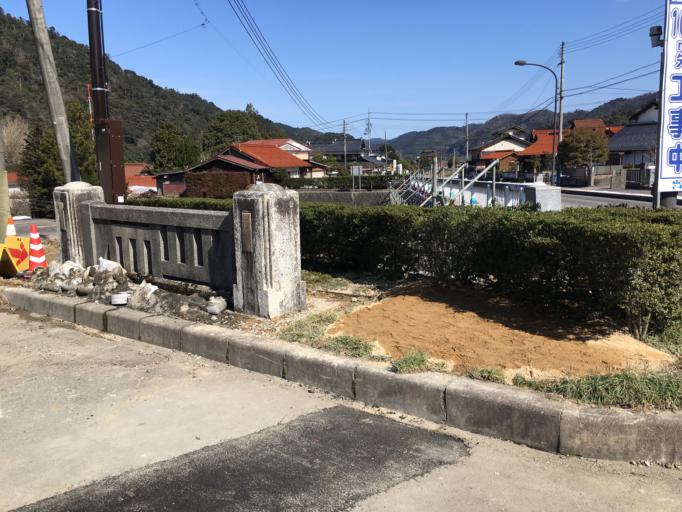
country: JP
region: Shimane
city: Masuda
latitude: 34.4533
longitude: 131.7670
